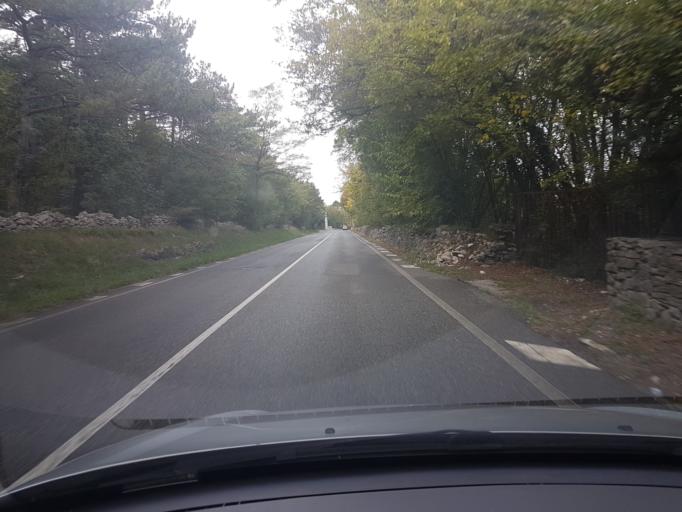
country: IT
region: Friuli Venezia Giulia
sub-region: Provincia di Trieste
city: Aurisina
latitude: 45.7436
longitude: 13.6808
